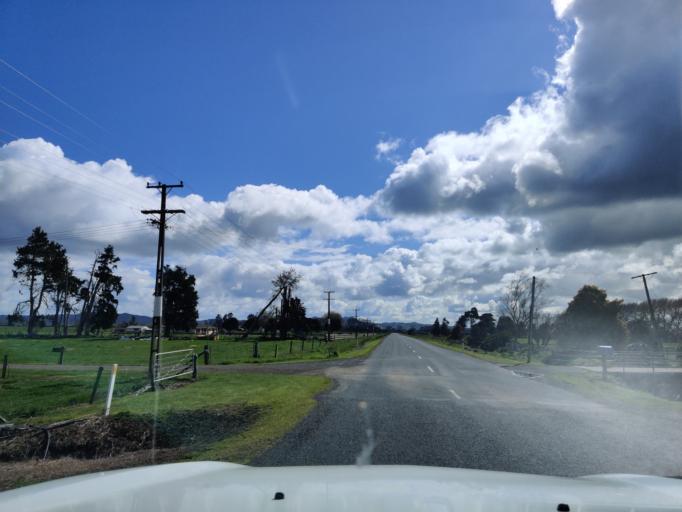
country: NZ
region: Waikato
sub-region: Waikato District
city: Ngaruawahia
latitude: -37.5940
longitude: 175.2938
